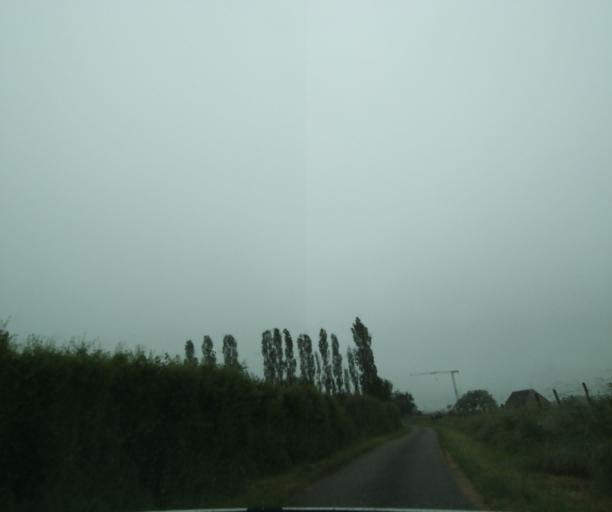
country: FR
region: Bourgogne
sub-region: Departement de Saone-et-Loire
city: Charolles
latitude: 46.3929
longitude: 4.2298
